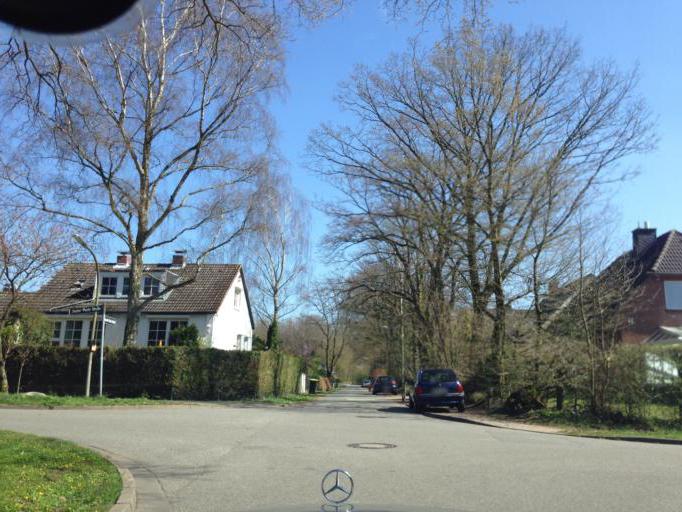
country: DE
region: Schleswig-Holstein
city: Barsbuettel
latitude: 53.5927
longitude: 10.1638
